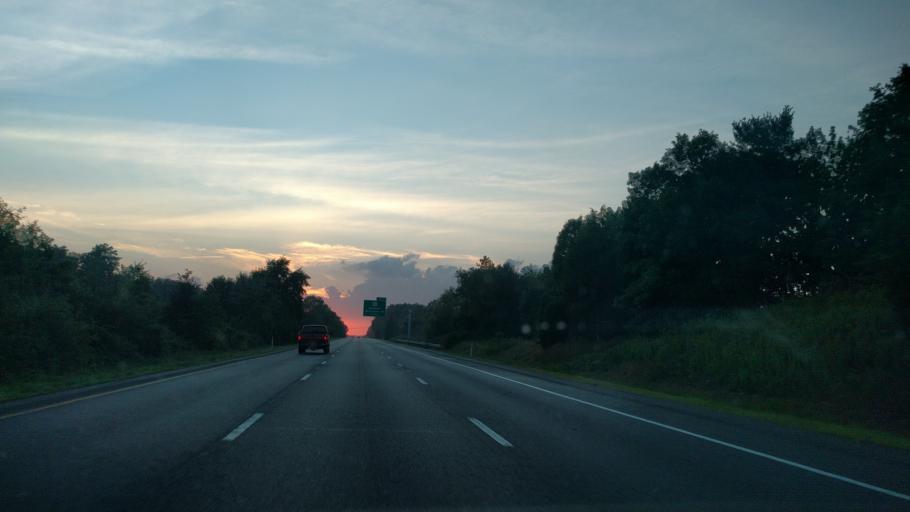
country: US
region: Massachusetts
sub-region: Bristol County
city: Seekonk
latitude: 41.7962
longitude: -71.3174
